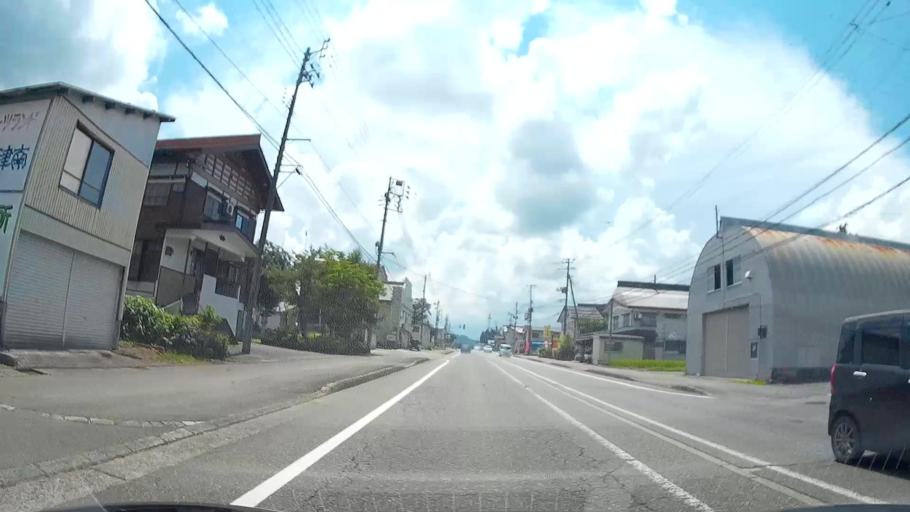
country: JP
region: Niigata
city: Tokamachi
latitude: 37.0337
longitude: 138.6707
